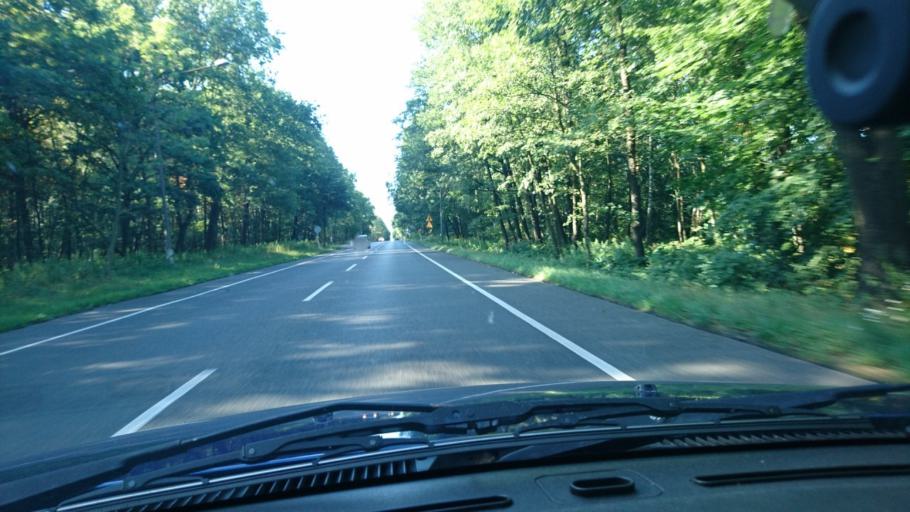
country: PL
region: Silesian Voivodeship
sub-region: Gliwice
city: Gliwice
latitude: 50.3357
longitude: 18.6554
